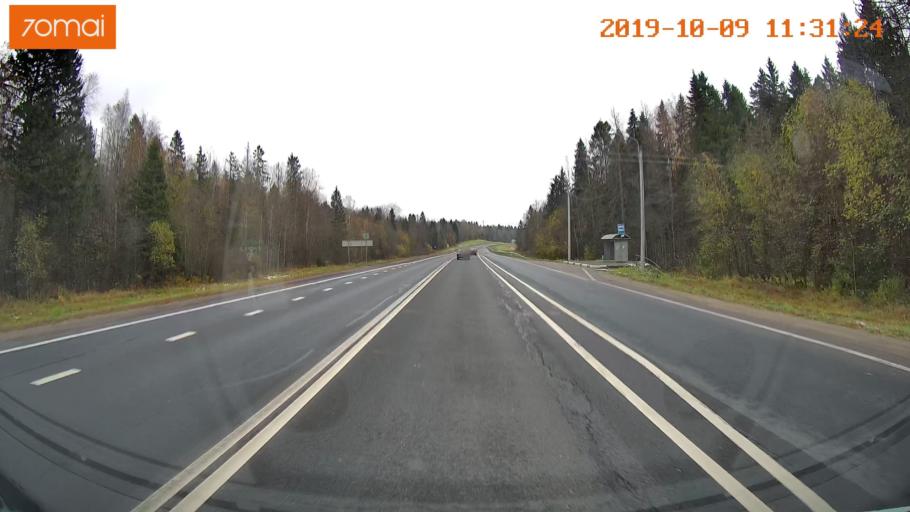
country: RU
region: Vologda
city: Gryazovets
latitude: 59.0461
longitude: 40.0947
